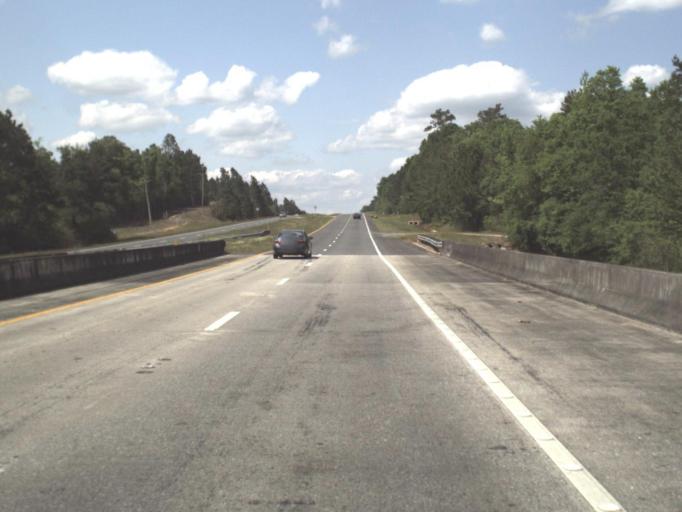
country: US
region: Florida
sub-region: Escambia County
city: Century
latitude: 30.8727
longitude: -87.3220
